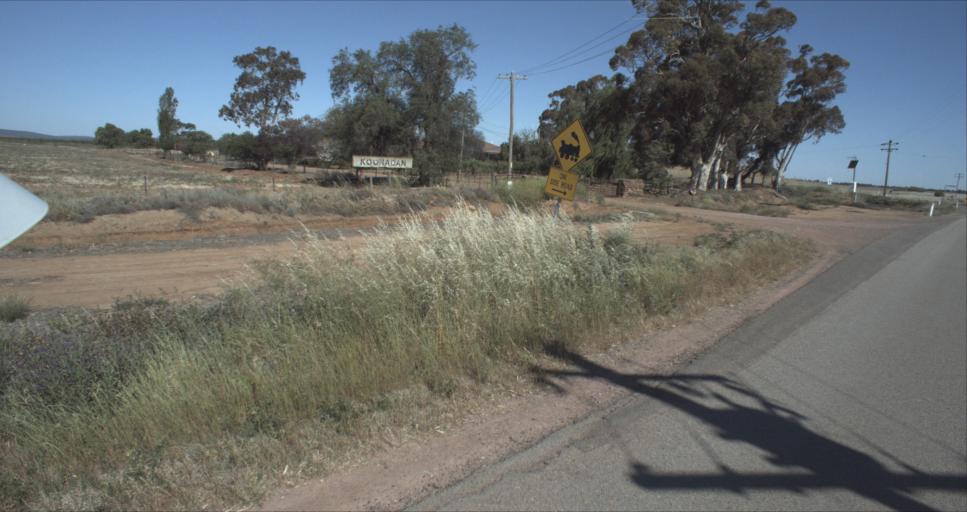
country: AU
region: New South Wales
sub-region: Leeton
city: Leeton
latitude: -34.4773
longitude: 146.3681
